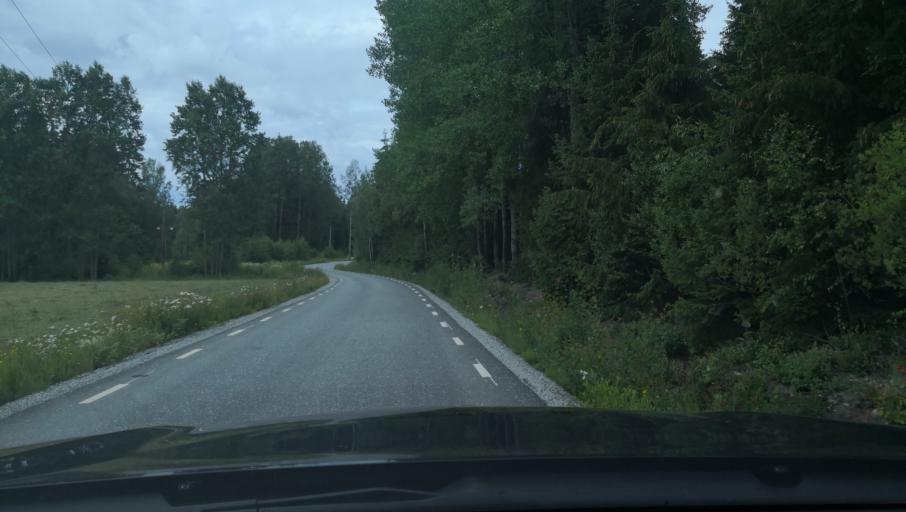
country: SE
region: Vaestmanland
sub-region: Hallstahammars Kommun
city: Hallstahammar
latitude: 59.6203
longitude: 16.1405
